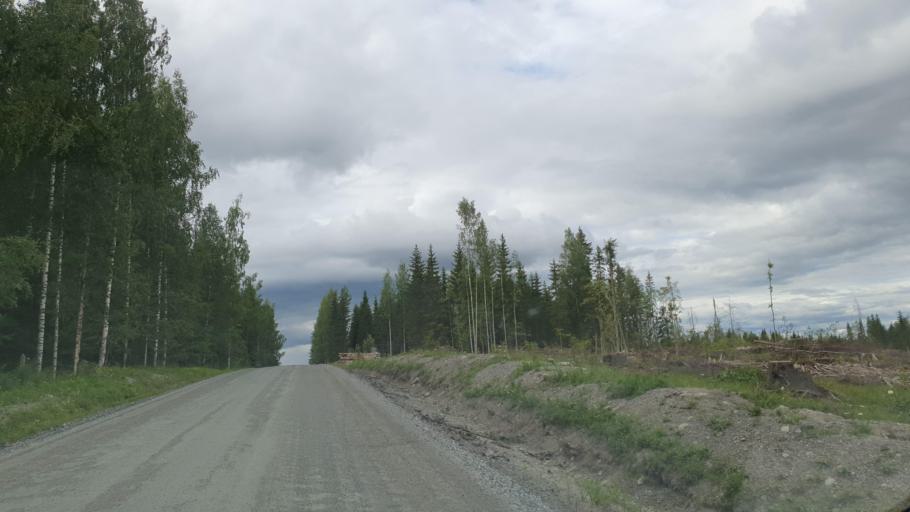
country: FI
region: Northern Savo
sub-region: Ylae-Savo
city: Iisalmi
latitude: 63.5235
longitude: 27.0939
